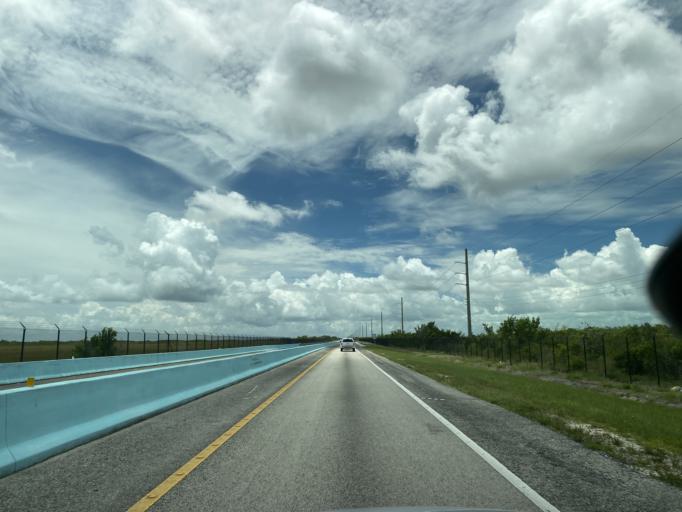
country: US
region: Florida
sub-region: Miami-Dade County
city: Florida City
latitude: 25.3666
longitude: -80.4615
